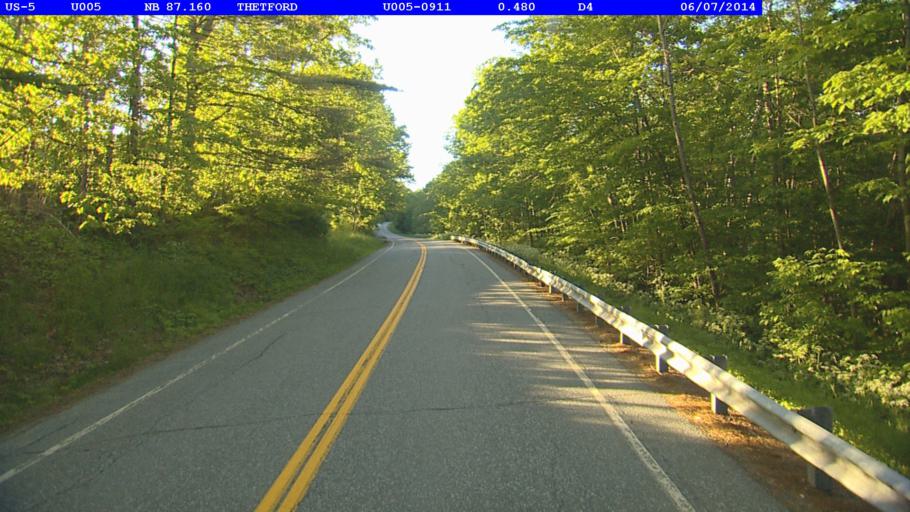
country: US
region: New Hampshire
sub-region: Grafton County
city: Lyme
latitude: 43.7786
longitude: -72.2057
